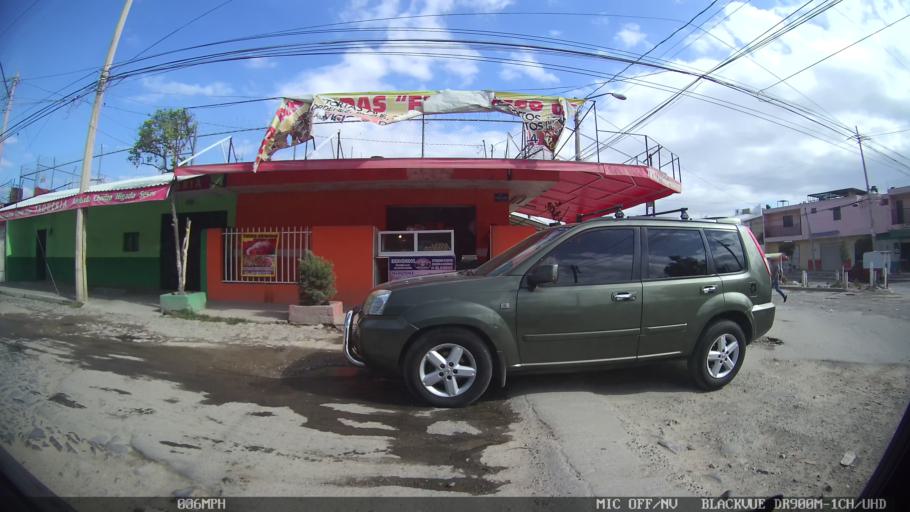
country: MX
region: Jalisco
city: Tonala
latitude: 20.6631
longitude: -103.2519
